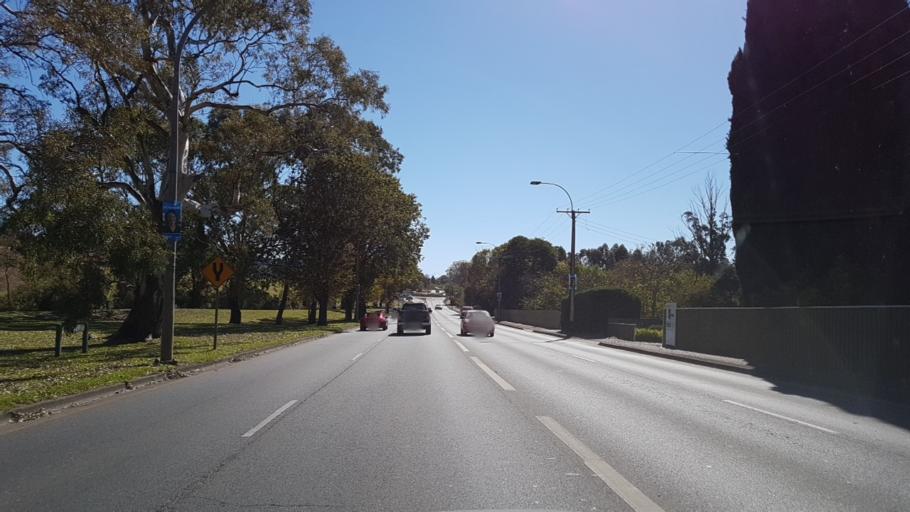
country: AU
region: South Australia
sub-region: Mount Barker
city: Mount Barker
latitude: -35.0718
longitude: 138.8572
